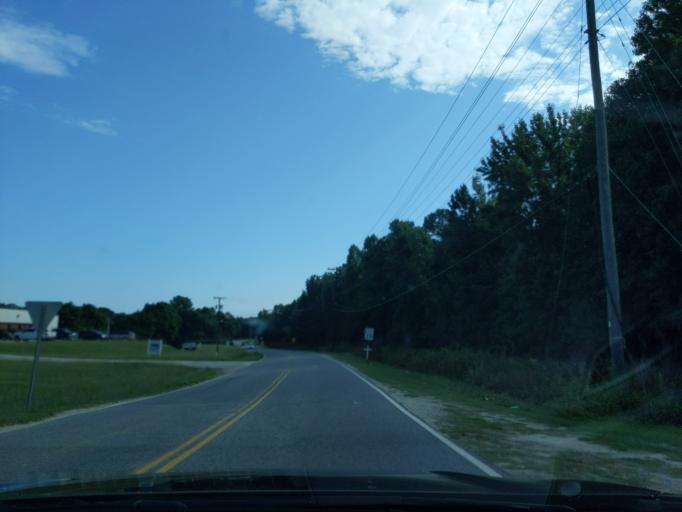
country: US
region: South Carolina
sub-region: Greenville County
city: Mauldin
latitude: 34.8031
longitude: -82.3122
